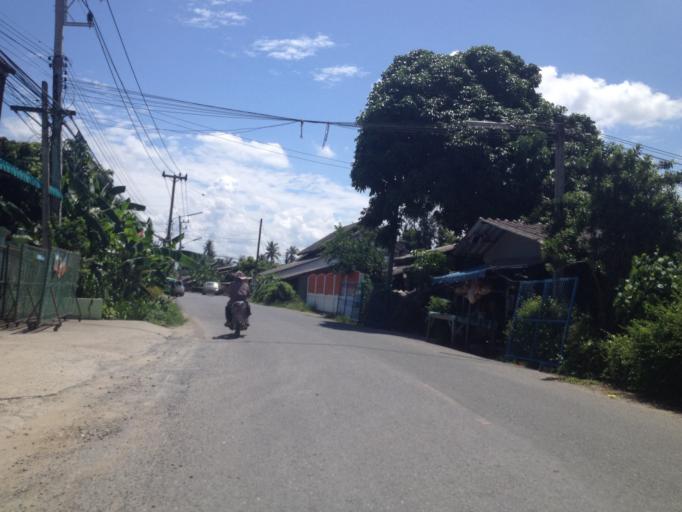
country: TH
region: Chiang Mai
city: Hang Dong
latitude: 18.6640
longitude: 98.9210
